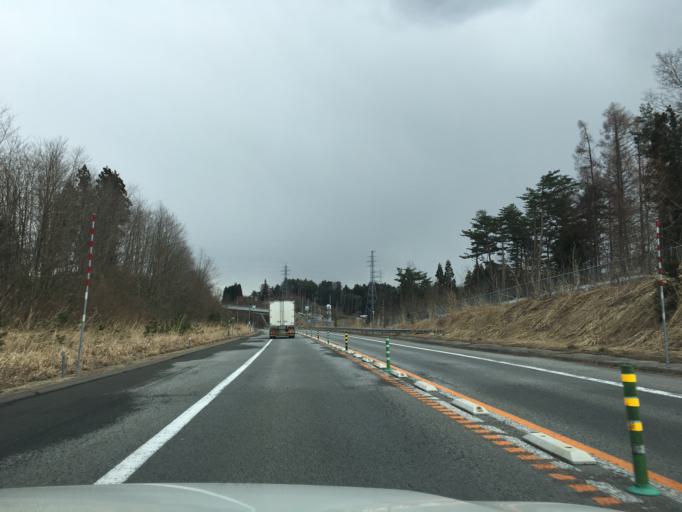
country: JP
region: Aomori
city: Aomori Shi
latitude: 40.8006
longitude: 140.6985
